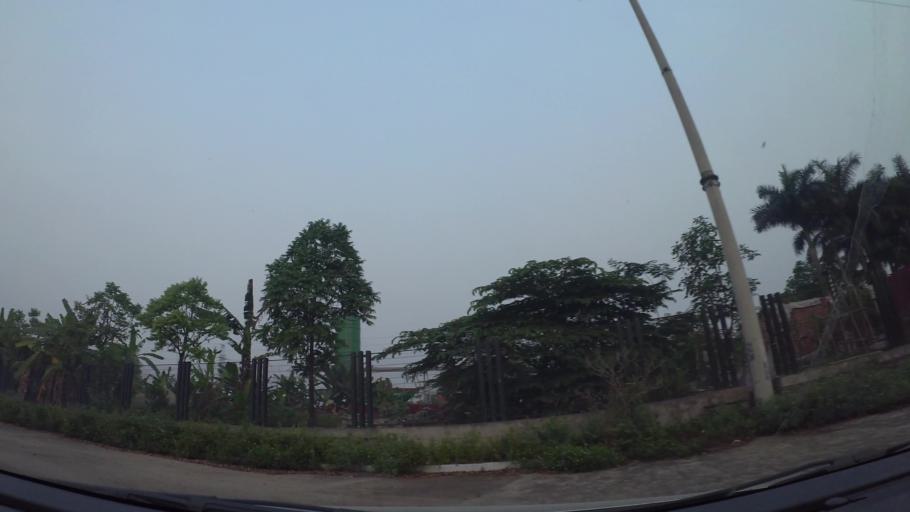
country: VN
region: Ha Noi
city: Ha Dong
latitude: 20.9940
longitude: 105.7340
